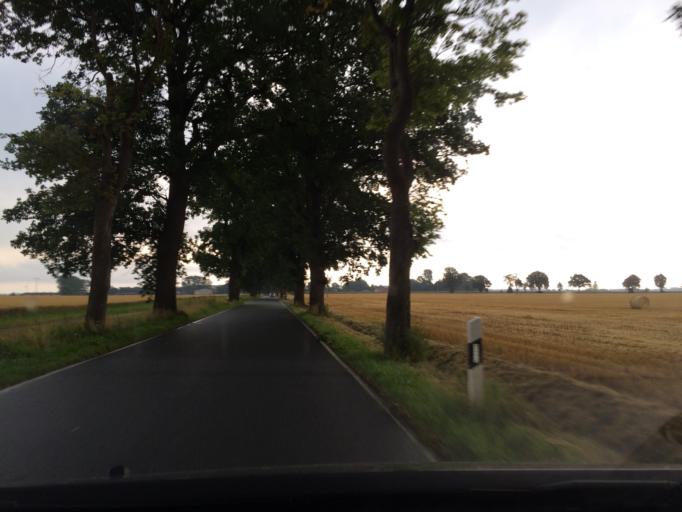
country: DE
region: Mecklenburg-Vorpommern
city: Preetz
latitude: 54.3494
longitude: 12.9955
